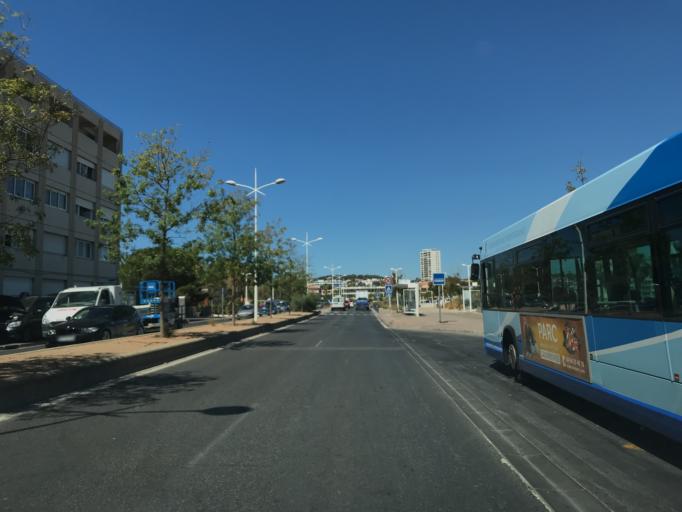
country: FR
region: Provence-Alpes-Cote d'Azur
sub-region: Departement du Var
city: La Seyne-sur-Mer
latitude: 43.0801
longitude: 5.8972
